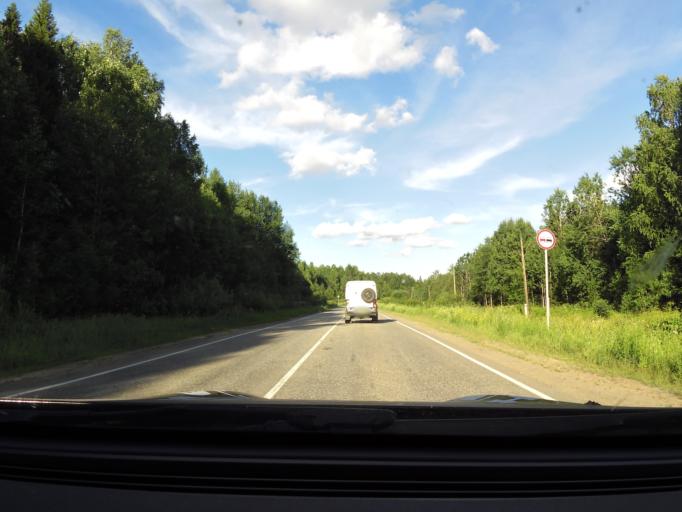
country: RU
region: Kirov
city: Belorechensk
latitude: 58.7159
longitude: 52.2922
